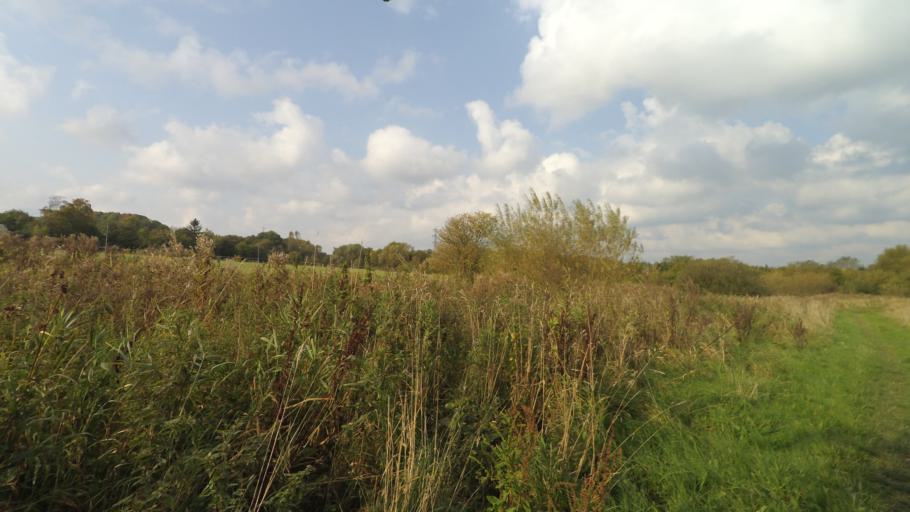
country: DK
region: Central Jutland
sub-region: Arhus Kommune
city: Stavtrup
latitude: 56.1269
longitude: 10.1372
